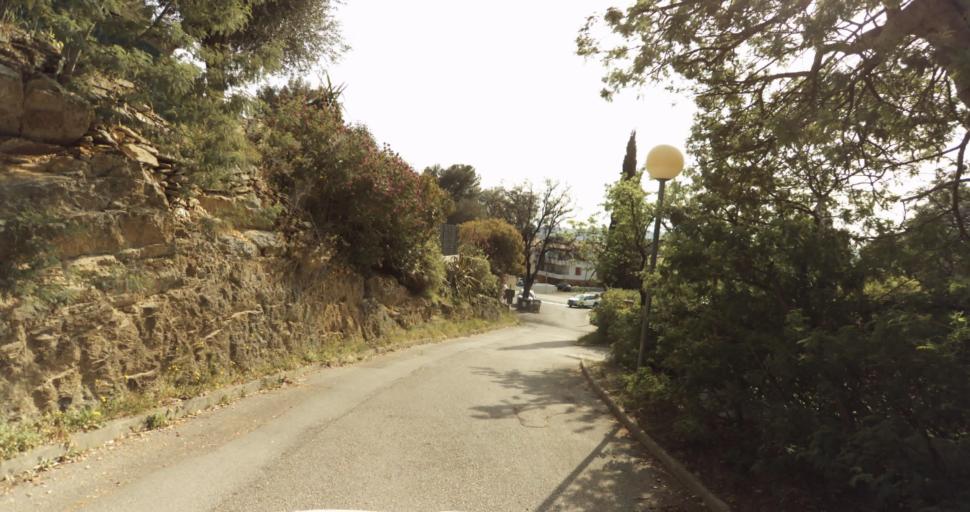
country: FR
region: Provence-Alpes-Cote d'Azur
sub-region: Departement du Var
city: Bormes-les-Mimosas
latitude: 43.1452
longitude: 6.3453
